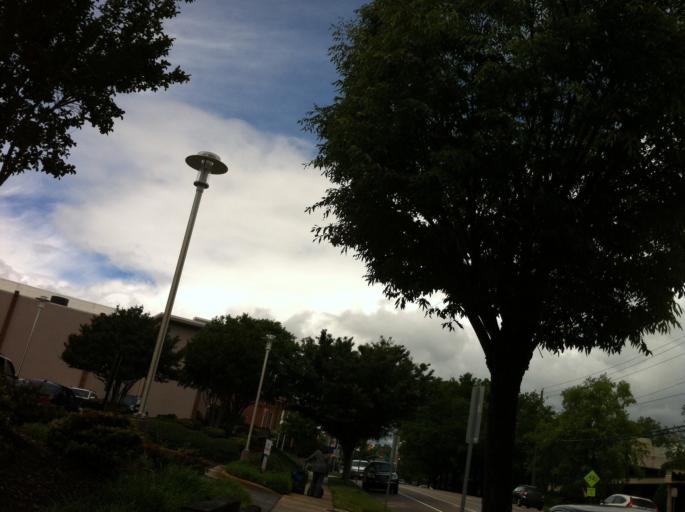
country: US
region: North Carolina
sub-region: Wake County
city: West Raleigh
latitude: 35.7848
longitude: -78.6594
